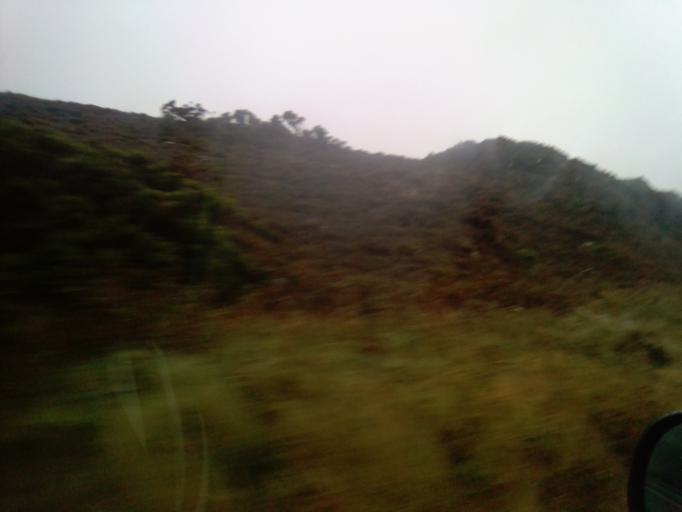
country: IE
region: Ulster
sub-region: County Donegal
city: Ramelton
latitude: 55.2634
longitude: -7.6409
